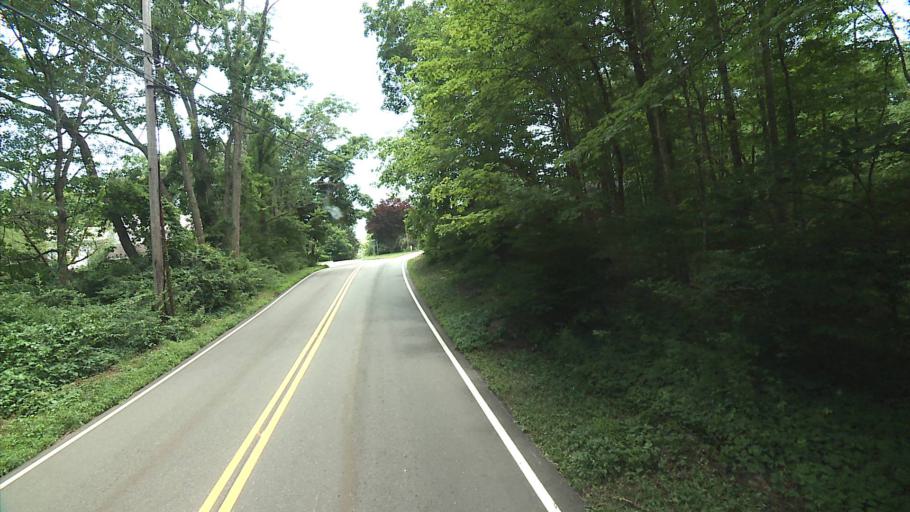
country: US
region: Connecticut
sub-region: New London County
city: Colchester
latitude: 41.4862
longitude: -72.3554
